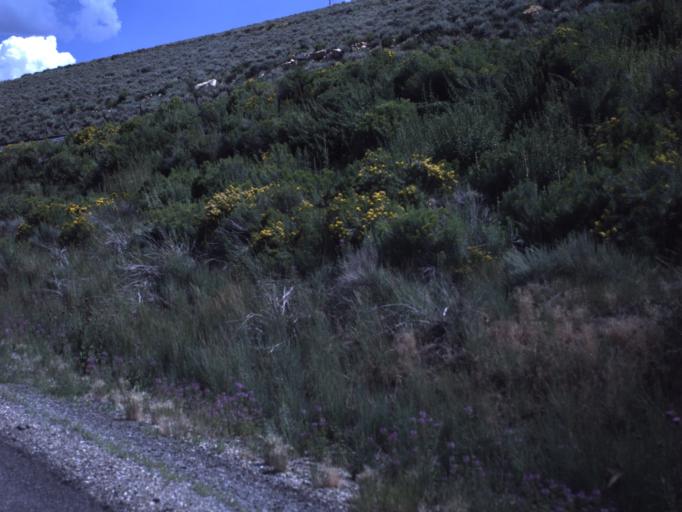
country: US
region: Utah
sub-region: Carbon County
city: Helper
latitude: 39.7444
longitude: -111.1512
